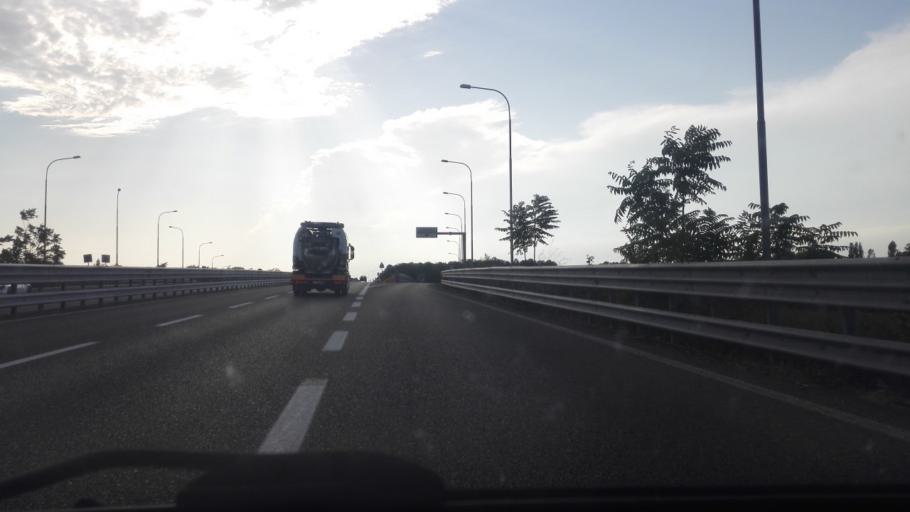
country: IT
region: Piedmont
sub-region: Provincia di Alessandria
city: Valle San Bartolomeo
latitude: 44.9334
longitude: 8.6294
